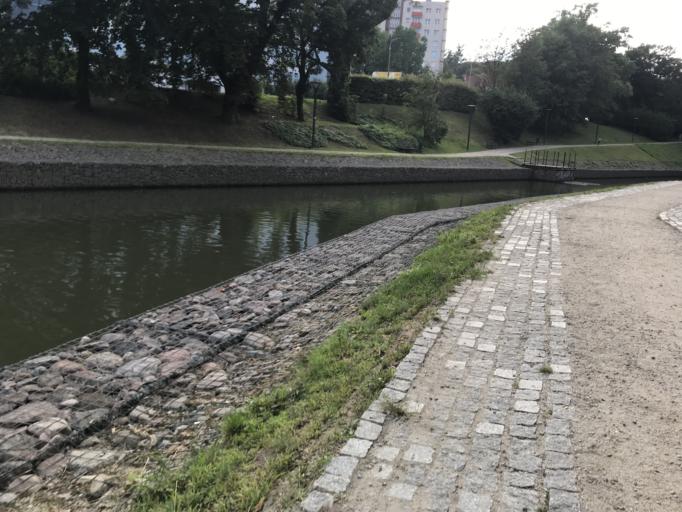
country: PL
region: Pomeranian Voivodeship
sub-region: Gdansk
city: Gdansk
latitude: 54.3523
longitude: 18.6369
